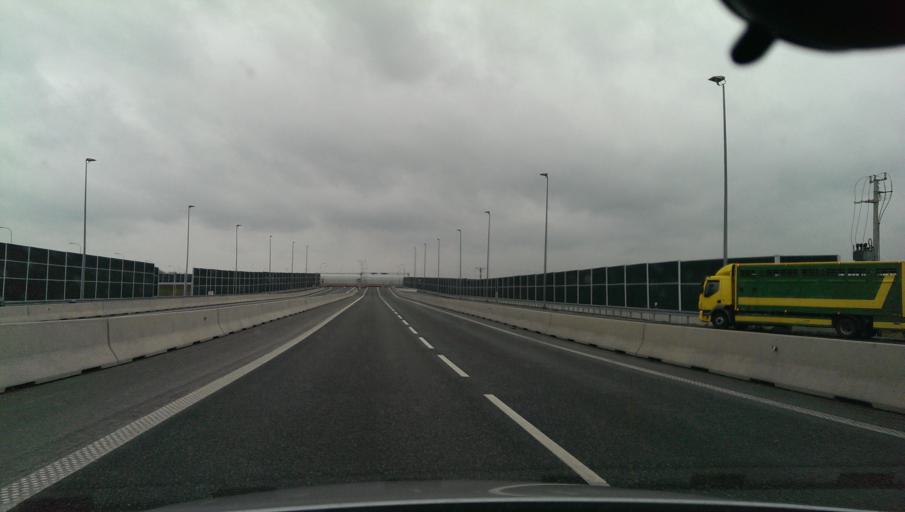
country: PL
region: Lesser Poland Voivodeship
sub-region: Powiat tarnowski
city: Wierzchoslawice
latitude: 50.0127
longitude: 20.8739
